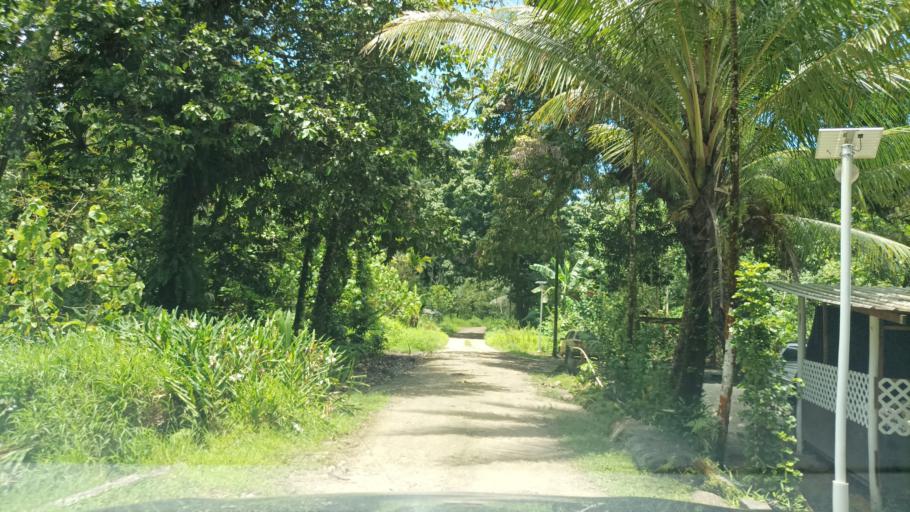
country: FM
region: Pohnpei
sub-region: Madolenihm Municipality
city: Madolenihm Municipality Government
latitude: 6.8443
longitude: 158.3178
